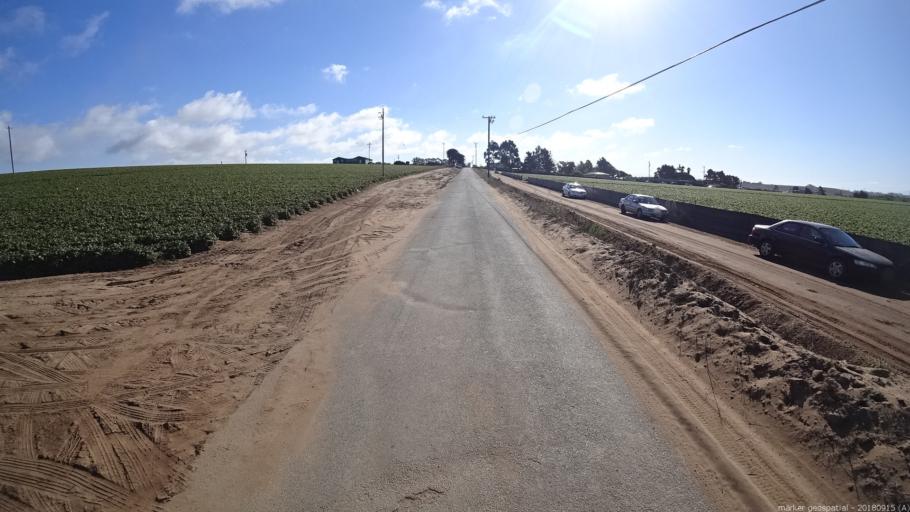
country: US
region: California
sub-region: Monterey County
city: Elkhorn
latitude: 36.8382
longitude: -121.7821
